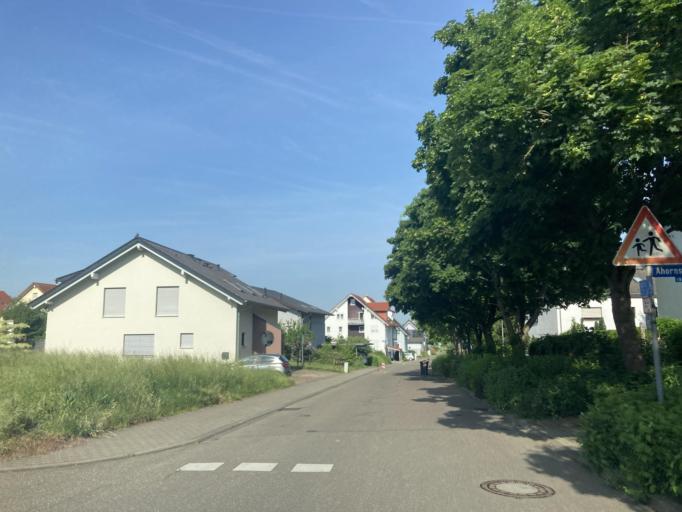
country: DE
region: Baden-Wuerttemberg
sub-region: Karlsruhe Region
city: Kronau
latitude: 49.2142
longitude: 8.6553
